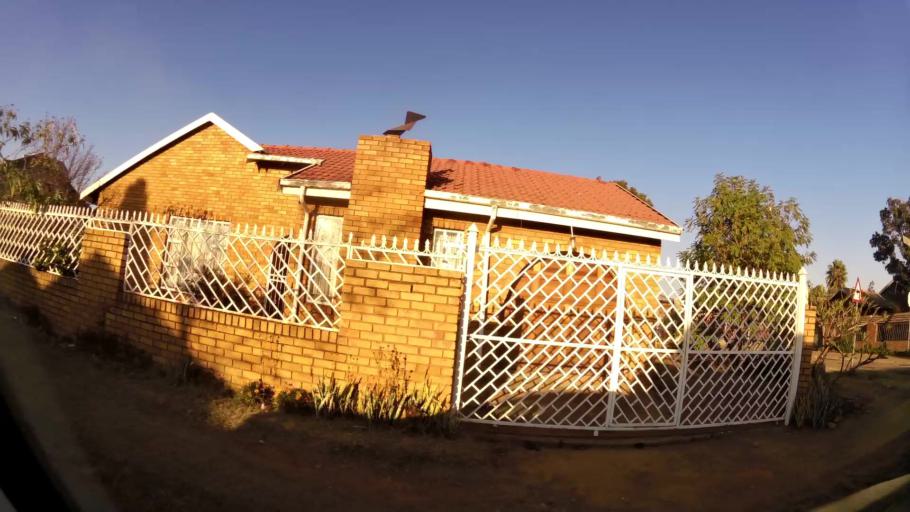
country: ZA
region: Gauteng
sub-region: City of Tshwane Metropolitan Municipality
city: Cullinan
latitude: -25.7243
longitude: 28.3906
